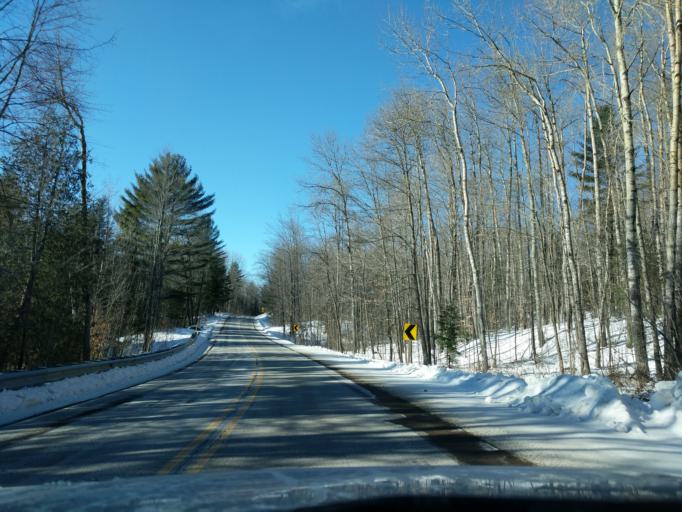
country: US
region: Wisconsin
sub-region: Menominee County
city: Keshena
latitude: 45.1129
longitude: -88.6428
